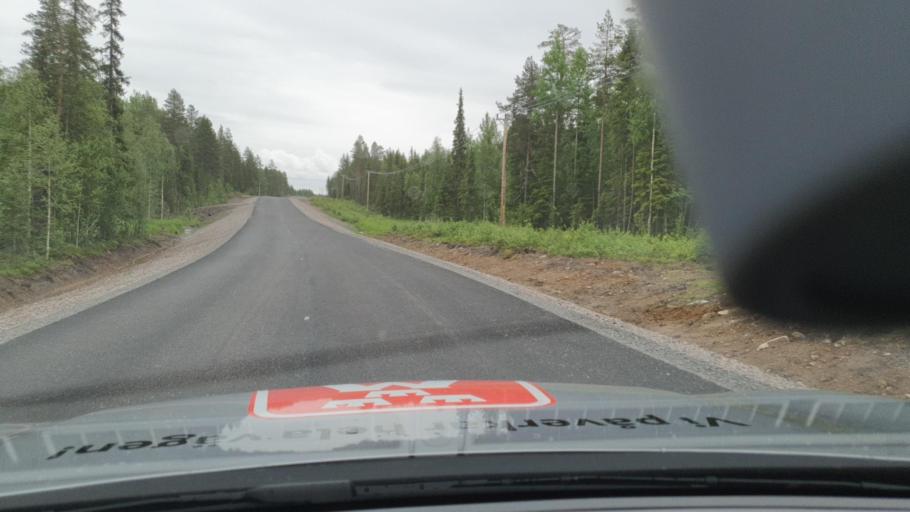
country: SE
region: Norrbotten
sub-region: Overtornea Kommun
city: OEvertornea
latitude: 66.6542
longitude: 23.2282
